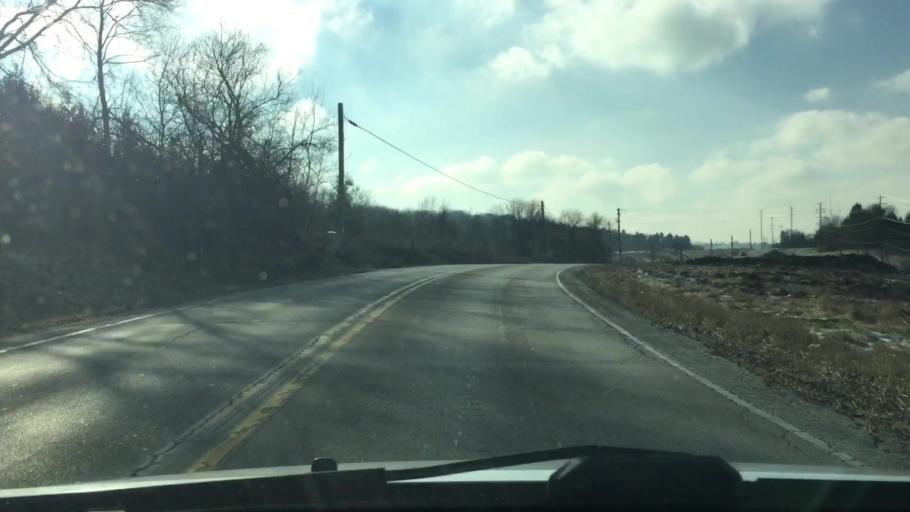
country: US
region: Wisconsin
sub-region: Waukesha County
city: Waukesha
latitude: 43.0121
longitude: -88.2860
